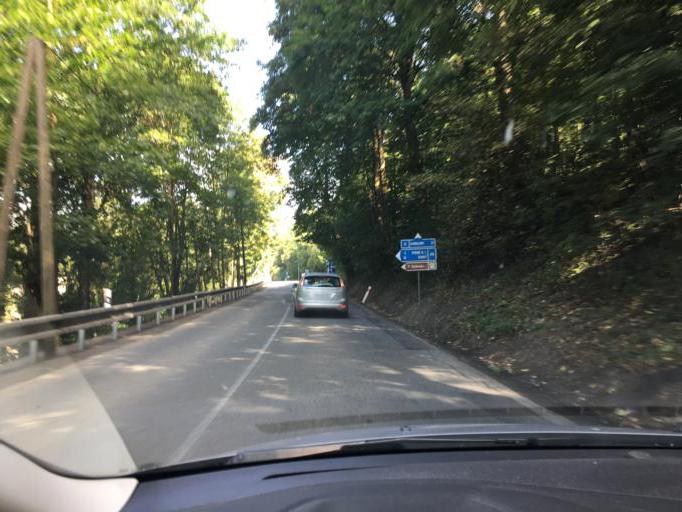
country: CZ
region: Liberecky
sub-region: Okres Semily
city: Ponikla
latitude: 50.6443
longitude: 15.4611
